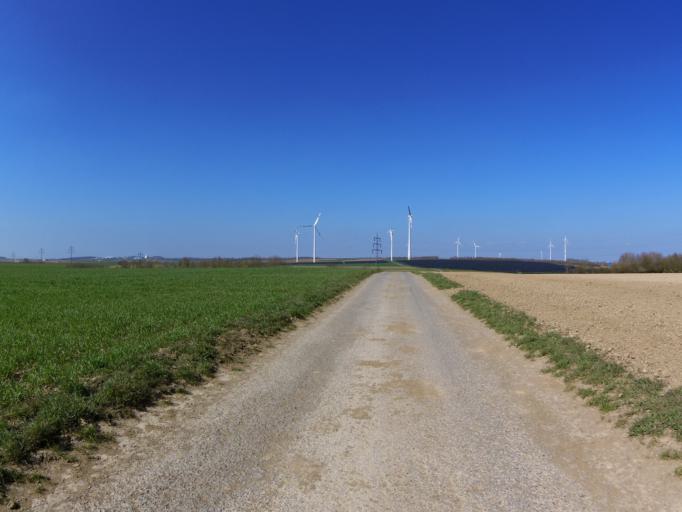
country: DE
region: Bavaria
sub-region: Regierungsbezirk Unterfranken
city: Biebelried
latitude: 49.7414
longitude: 10.1011
